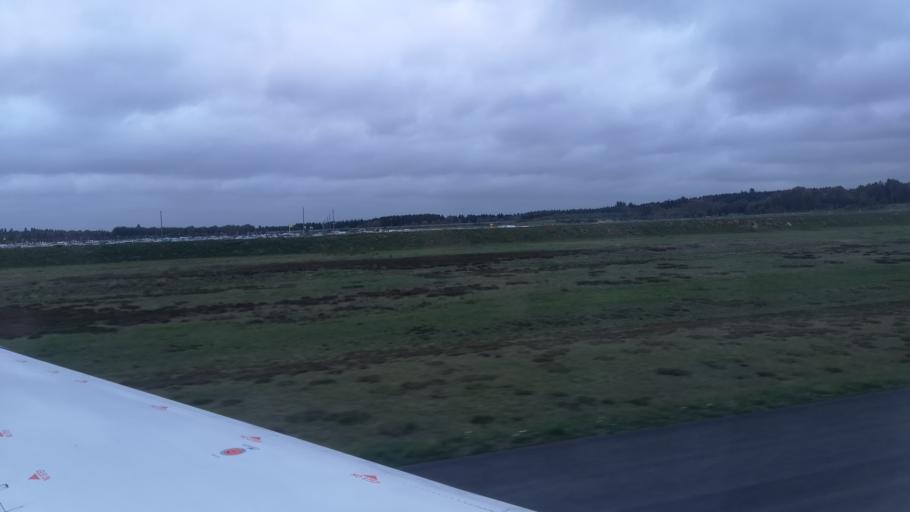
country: DK
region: South Denmark
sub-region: Billund Kommune
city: Billund
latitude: 55.7422
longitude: 9.1565
